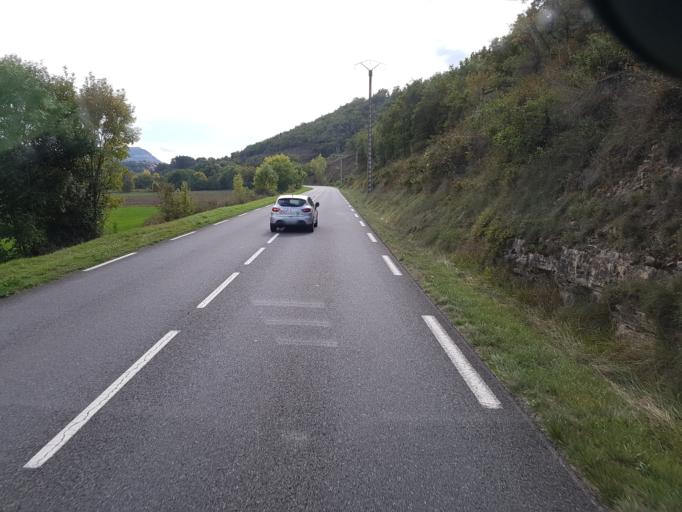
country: FR
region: Midi-Pyrenees
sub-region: Departement de l'Aveyron
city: Saint-Georges-de-Luzencon
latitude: 44.0248
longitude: 2.9644
